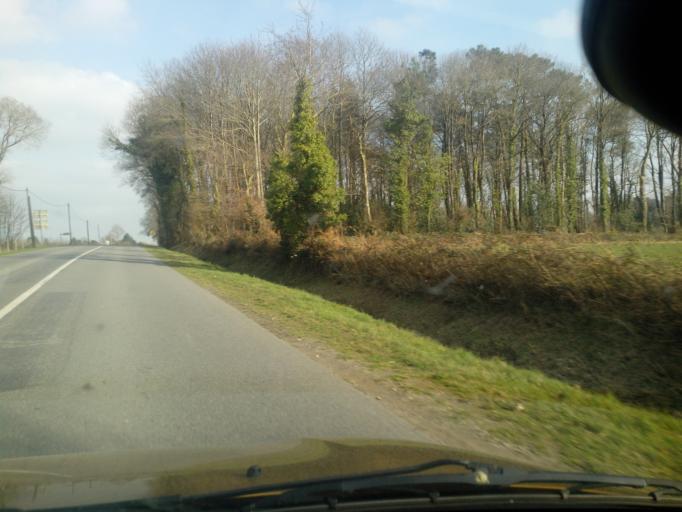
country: FR
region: Brittany
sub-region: Departement du Morbihan
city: La Vraie-Croix
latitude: 47.6970
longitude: -2.5156
